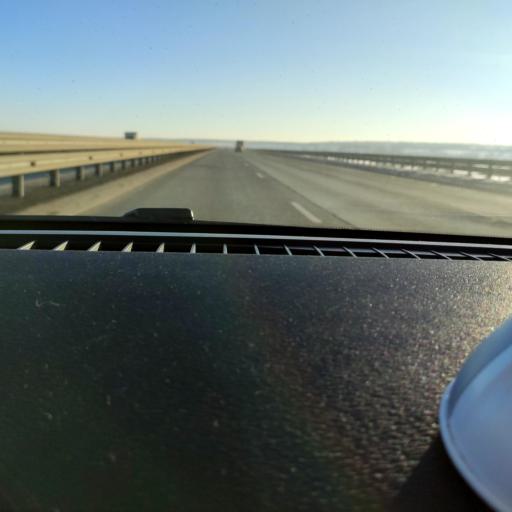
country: RU
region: Samara
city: Smyshlyayevka
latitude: 53.1577
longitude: 50.3357
